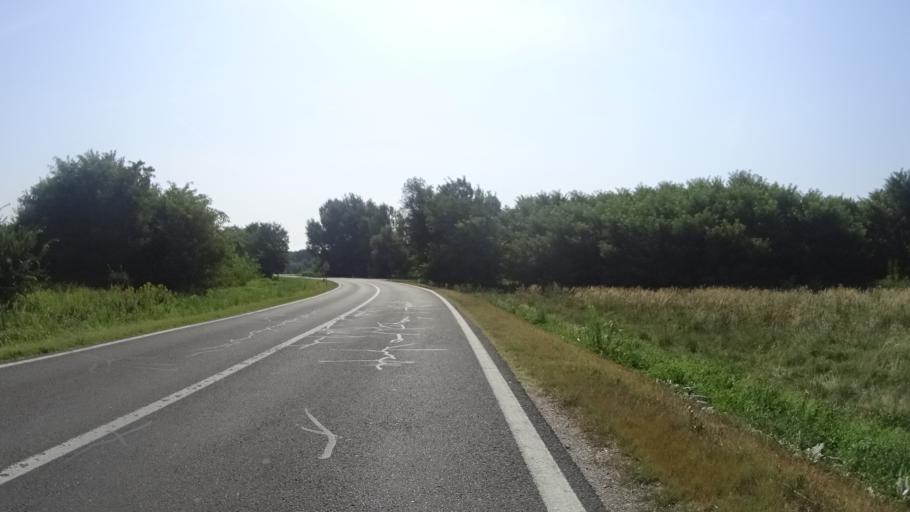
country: HR
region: Medimurska
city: Palovec
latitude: 46.3873
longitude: 16.5623
